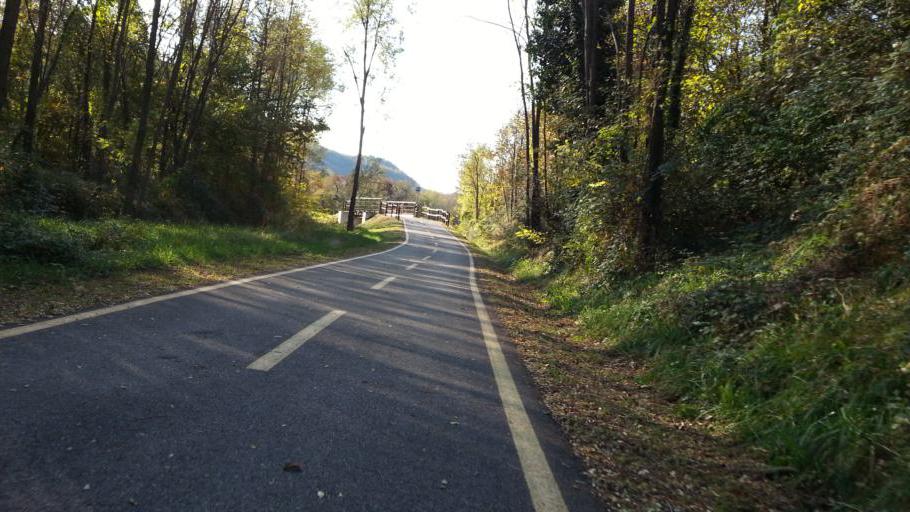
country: IT
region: Friuli Venezia Giulia
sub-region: Provincia di Udine
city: Venzone
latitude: 46.3200
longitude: 13.1300
